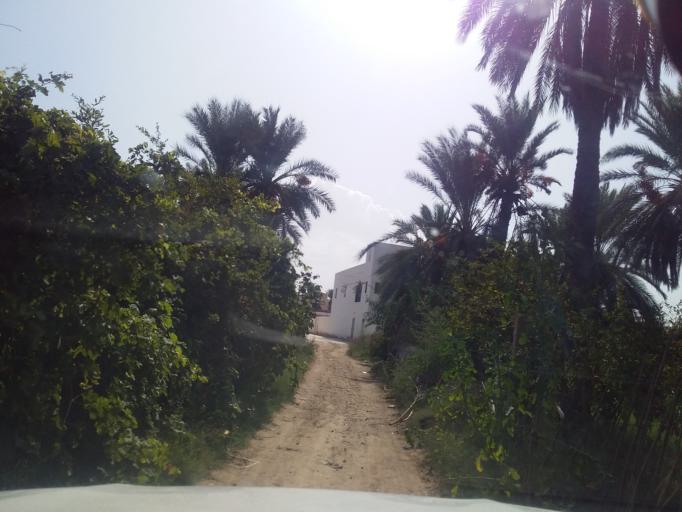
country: TN
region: Qabis
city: Gabes
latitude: 33.6240
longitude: 10.2869
